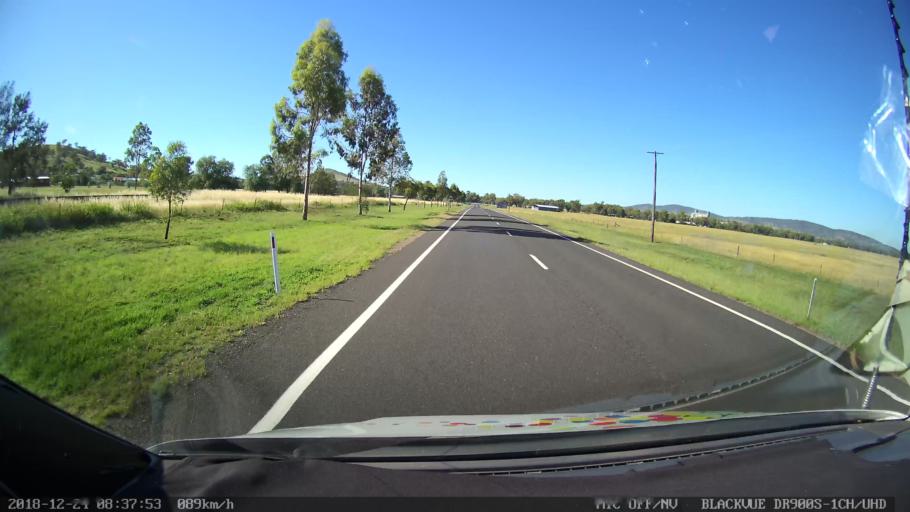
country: AU
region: New South Wales
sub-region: Liverpool Plains
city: Quirindi
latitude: -31.3352
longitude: 150.6480
